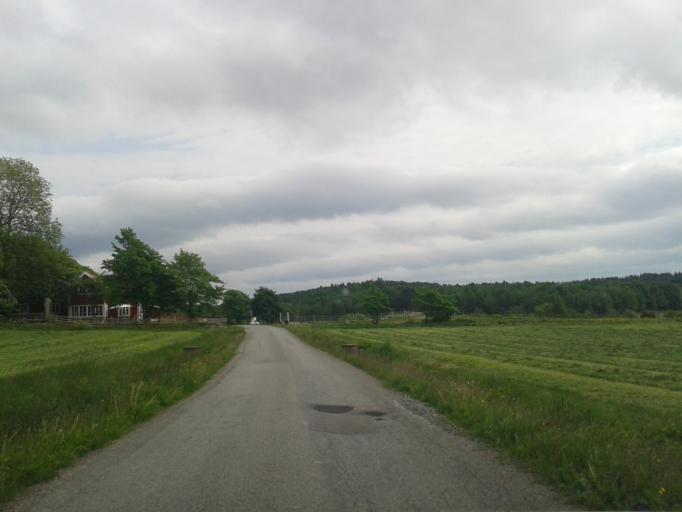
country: SE
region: Vaestra Goetaland
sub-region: Kungalvs Kommun
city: Kungalv
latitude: 57.9036
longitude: 11.9528
